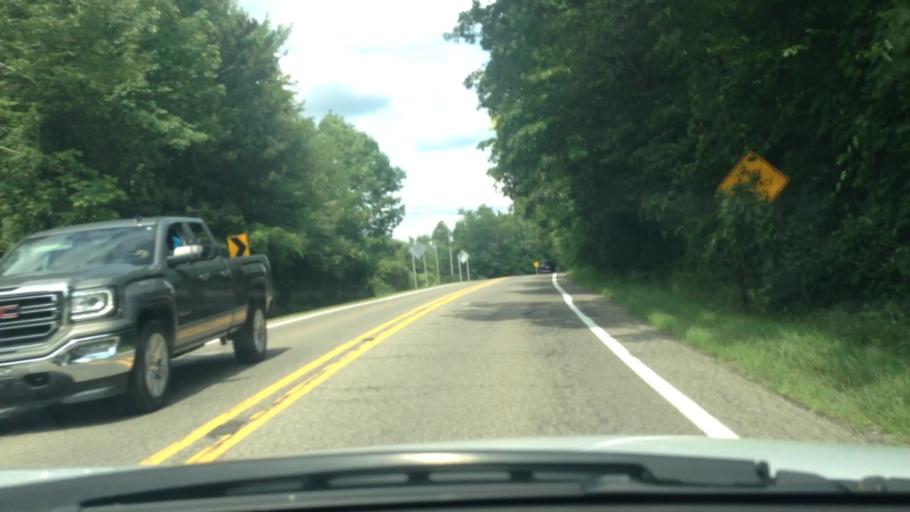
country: US
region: Michigan
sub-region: Oakland County
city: Clarkston
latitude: 42.7505
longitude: -83.3966
